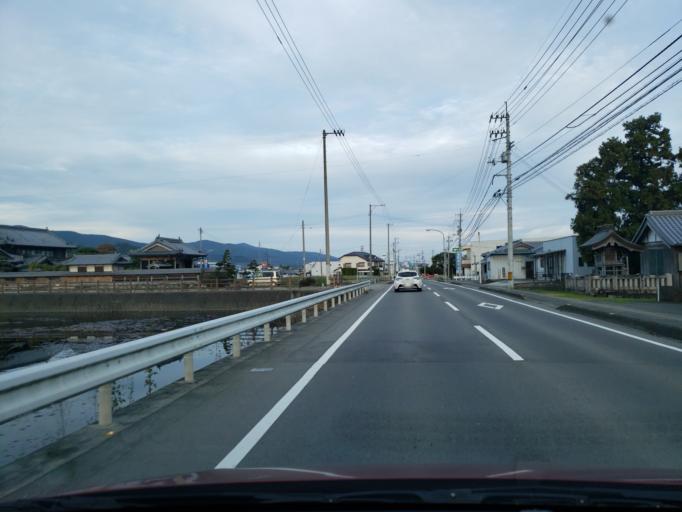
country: JP
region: Tokushima
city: Kamojimacho-jogejima
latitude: 34.0895
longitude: 134.2999
